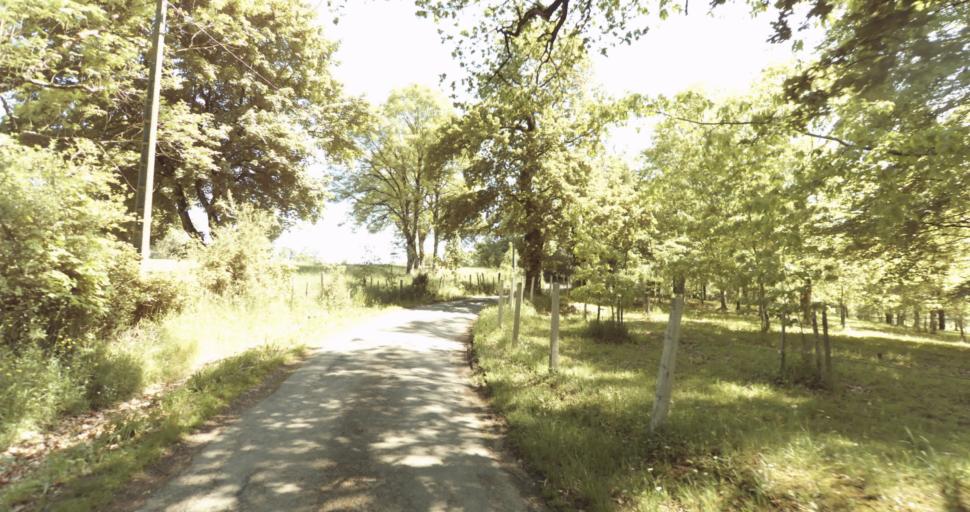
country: FR
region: Limousin
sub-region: Departement de la Haute-Vienne
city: Le Vigen
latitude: 45.7521
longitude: 1.2990
